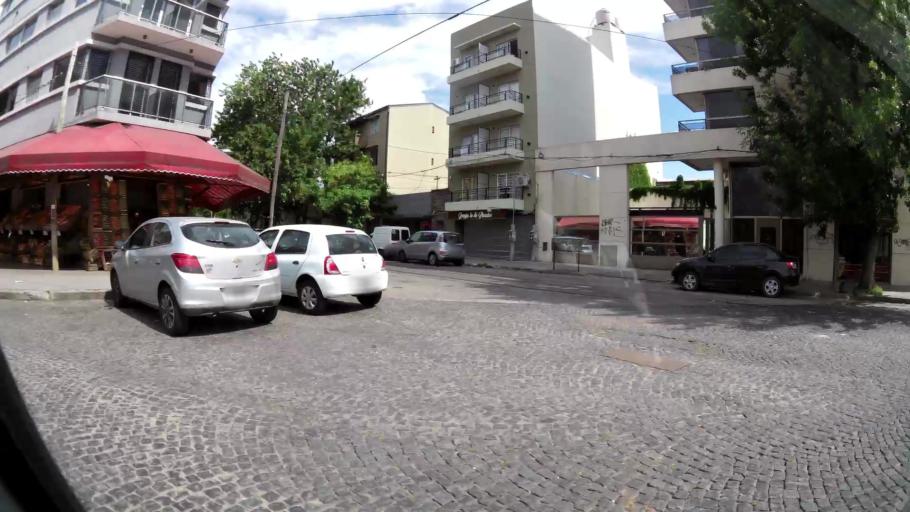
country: AR
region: Buenos Aires
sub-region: Partido de La Plata
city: La Plata
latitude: -34.9206
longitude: -57.9327
